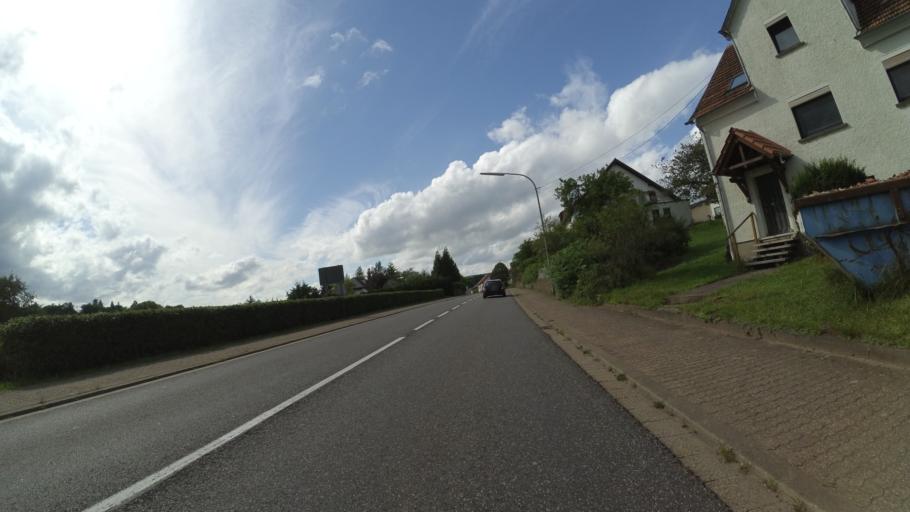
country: DE
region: Saarland
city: Tholey
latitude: 49.5373
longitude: 6.9877
